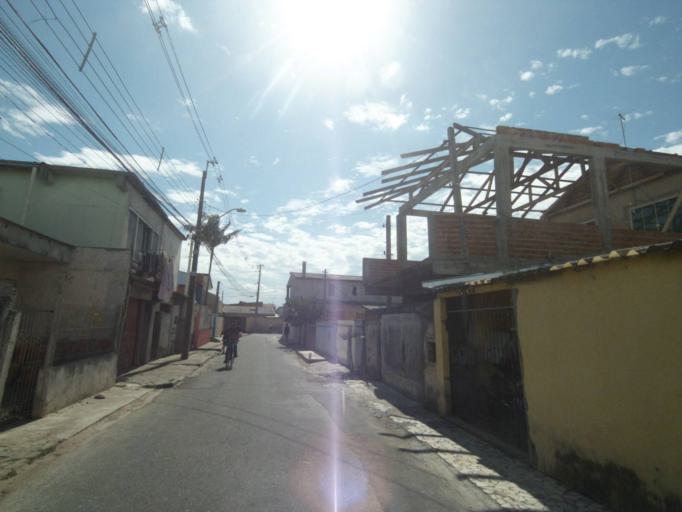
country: BR
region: Parana
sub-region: Curitiba
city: Curitiba
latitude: -25.5160
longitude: -49.3319
